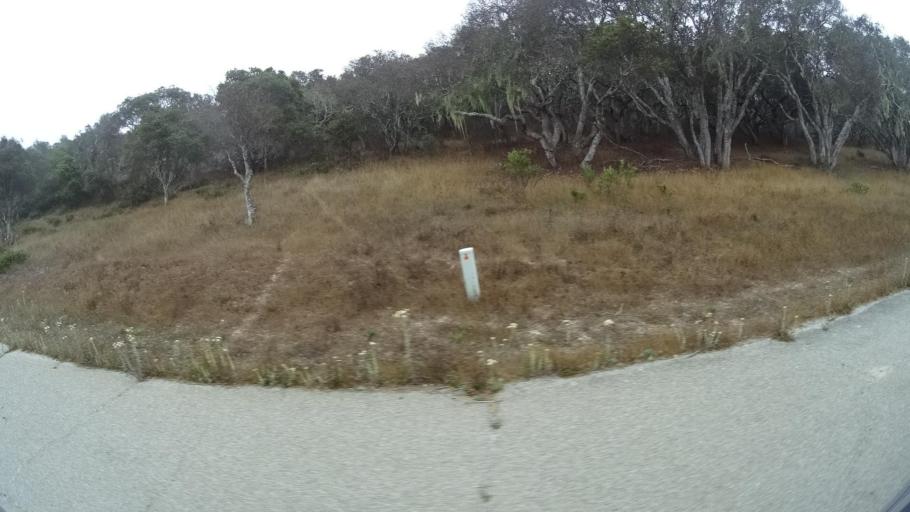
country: US
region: California
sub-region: Monterey County
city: Marina
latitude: 36.6489
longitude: -121.7545
